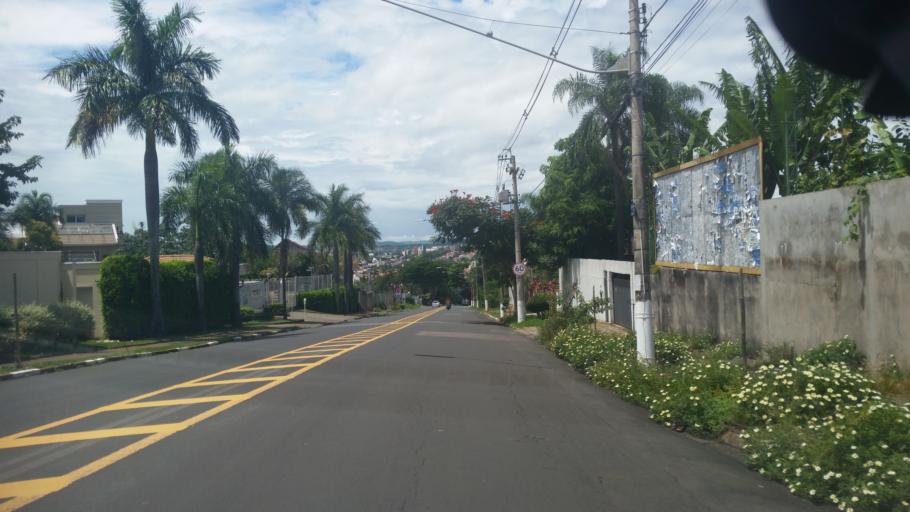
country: BR
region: Sao Paulo
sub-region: Campinas
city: Campinas
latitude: -22.8674
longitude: -47.0533
